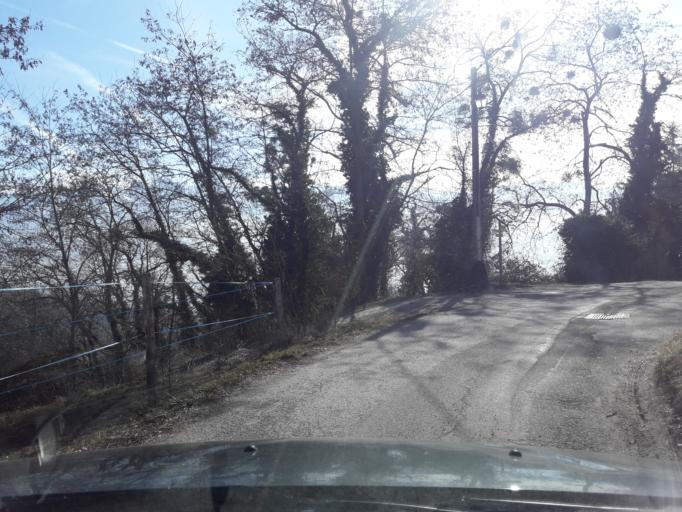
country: FR
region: Rhone-Alpes
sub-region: Departement de l'Isere
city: La Tronche
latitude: 45.2237
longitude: 5.7497
